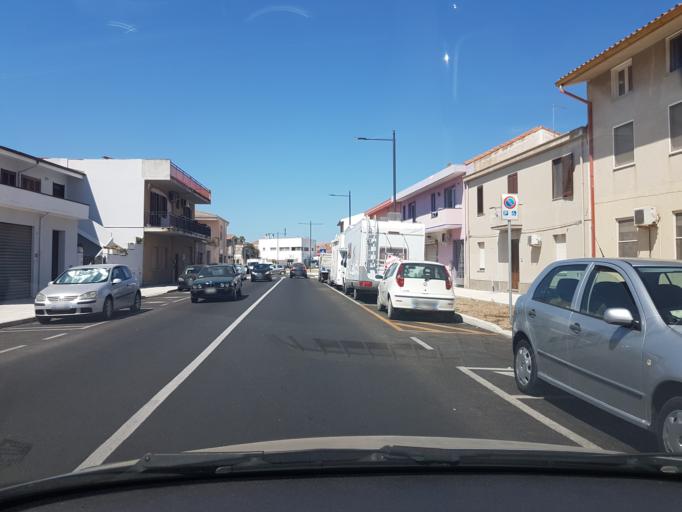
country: IT
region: Sardinia
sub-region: Provincia di Oristano
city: Oristano
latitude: 39.9003
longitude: 8.5991
